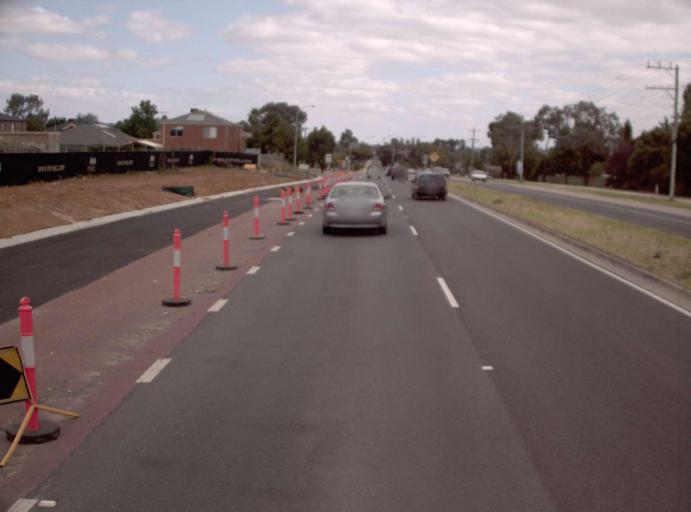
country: AU
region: Victoria
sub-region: Knox
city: Scoresby
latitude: -37.8868
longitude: 145.2330
